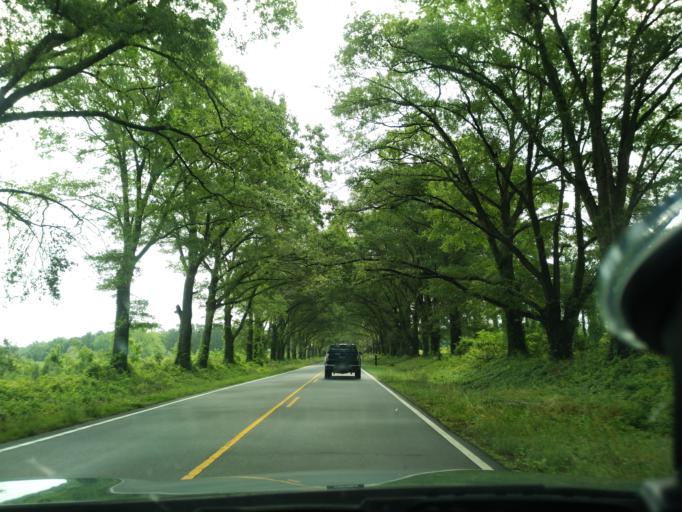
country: US
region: North Carolina
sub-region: Washington County
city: Plymouth
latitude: 35.9043
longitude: -76.6801
